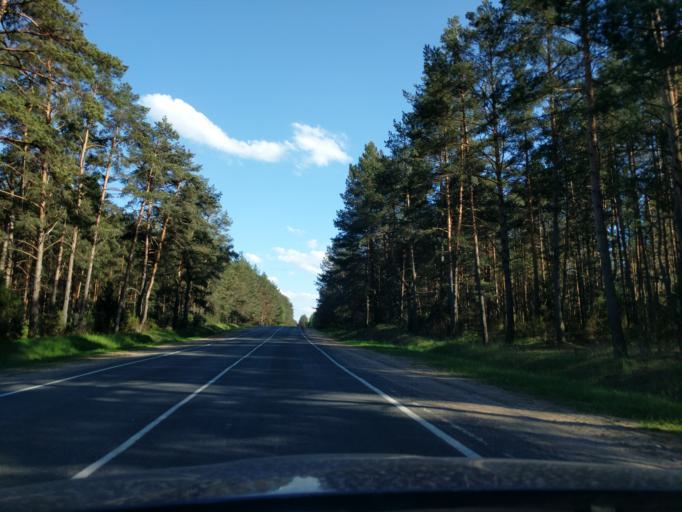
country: BY
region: Minsk
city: Myadzyel
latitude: 54.8414
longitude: 26.9282
